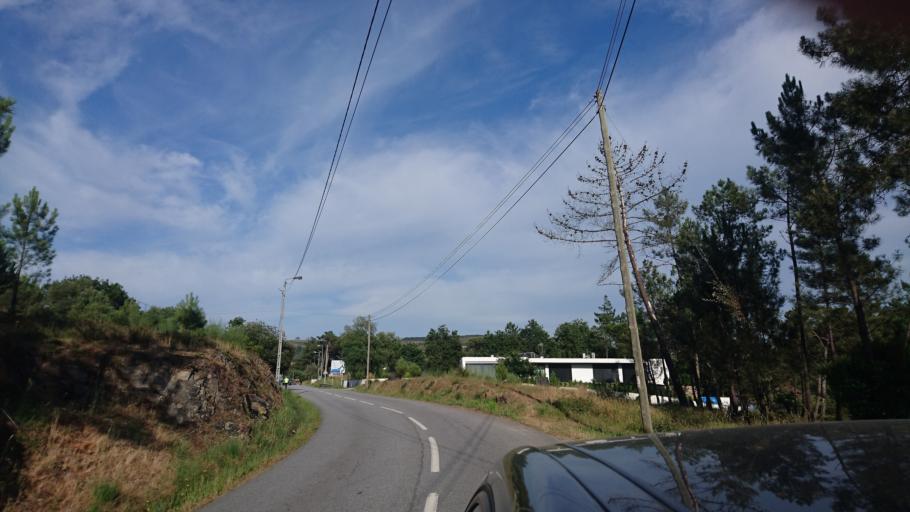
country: PT
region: Porto
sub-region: Paredes
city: Recarei
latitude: 41.1335
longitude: -8.4232
